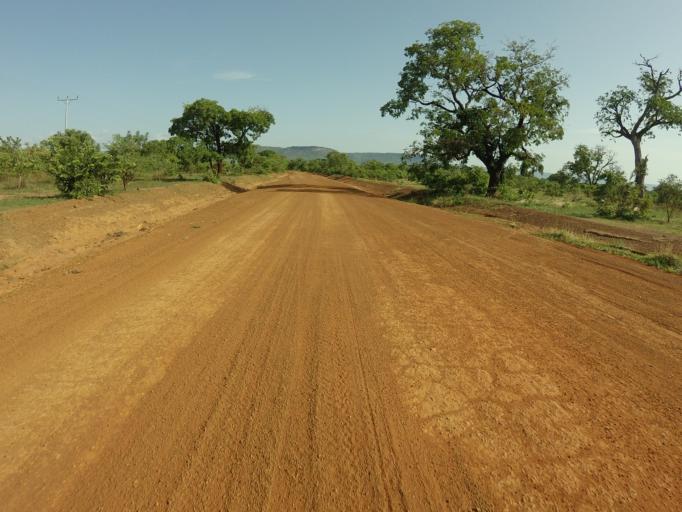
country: GH
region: Upper East
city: Bawku
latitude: 10.6909
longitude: -0.2158
